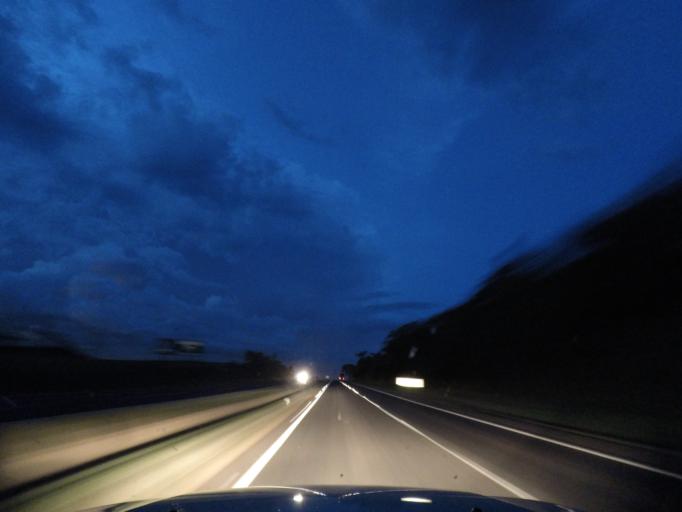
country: BR
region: Minas Gerais
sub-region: Uberlandia
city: Uberlandia
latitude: -19.2296
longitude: -48.1430
